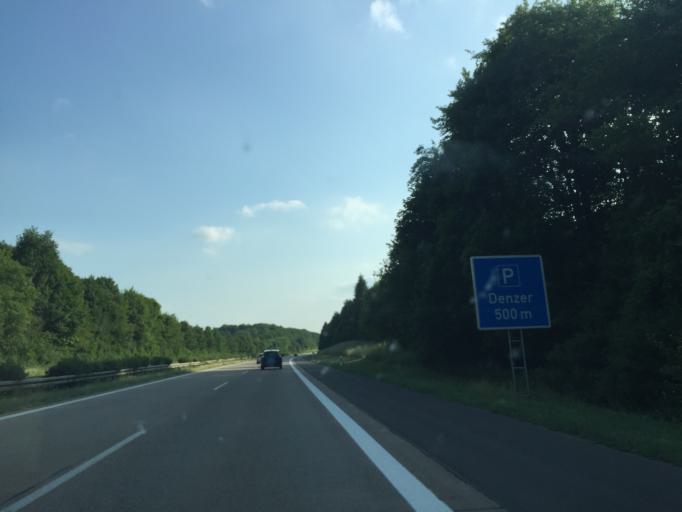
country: DE
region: Baden-Wuerttemberg
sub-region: Karlsruhe Region
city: Osterburken
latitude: 49.3863
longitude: 9.4658
